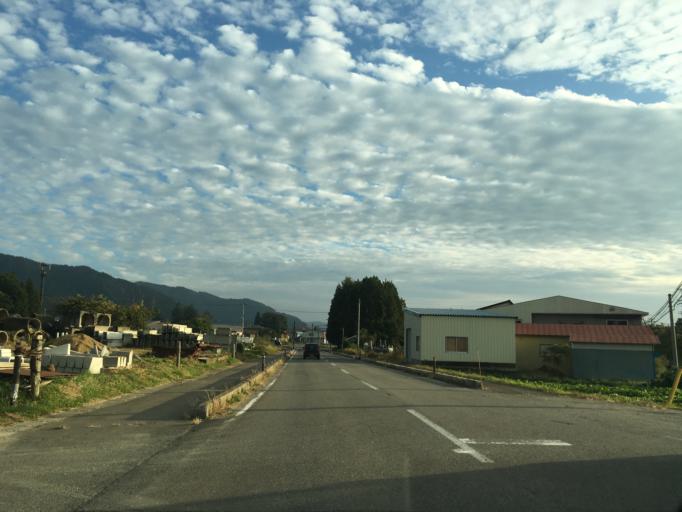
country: JP
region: Fukushima
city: Inawashiro
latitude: 37.5427
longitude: 140.1380
